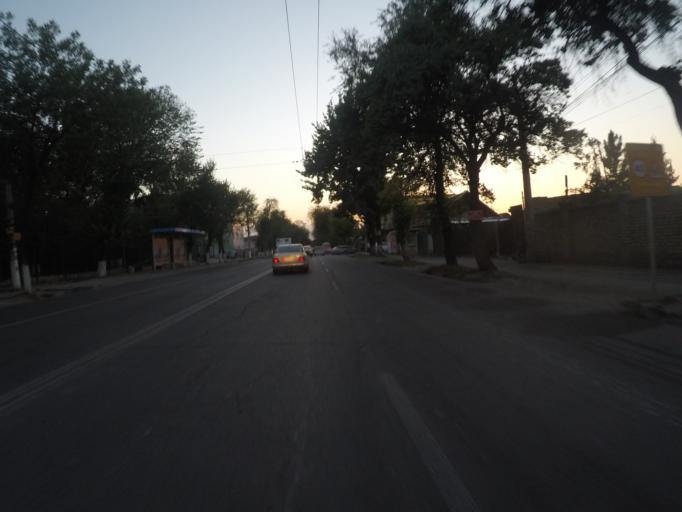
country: KG
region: Chuy
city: Bishkek
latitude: 42.8571
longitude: 74.6052
